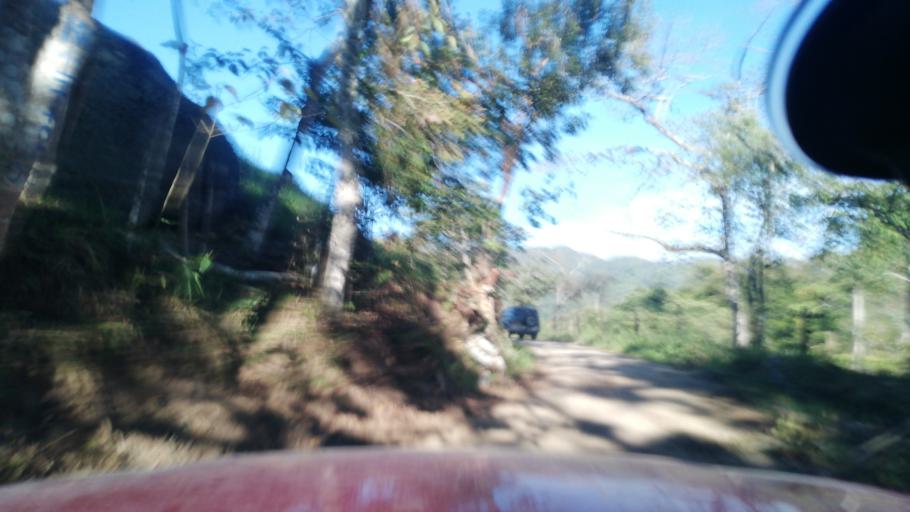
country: CO
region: Cundinamarca
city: Viani
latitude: 4.8202
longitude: -74.6152
